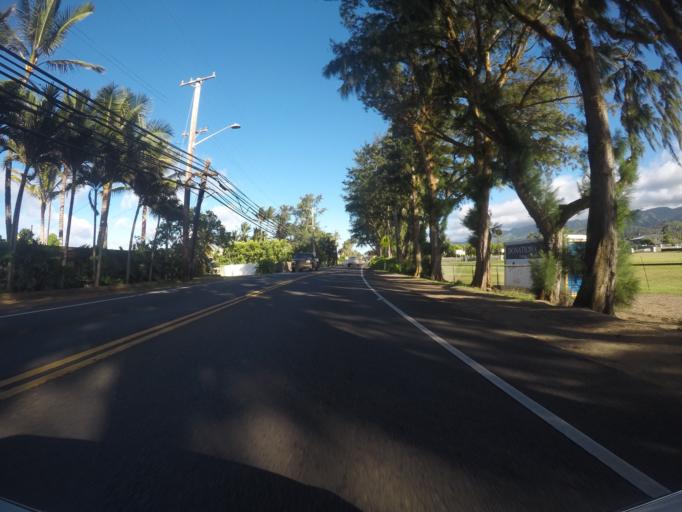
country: US
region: Hawaii
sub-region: Honolulu County
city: La'ie
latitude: 21.6500
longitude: -157.9242
